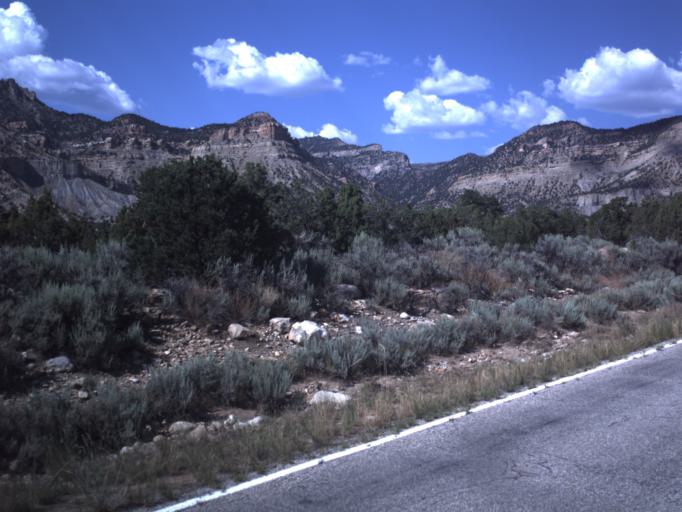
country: US
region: Utah
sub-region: Carbon County
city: Helper
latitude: 39.6756
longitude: -110.8166
